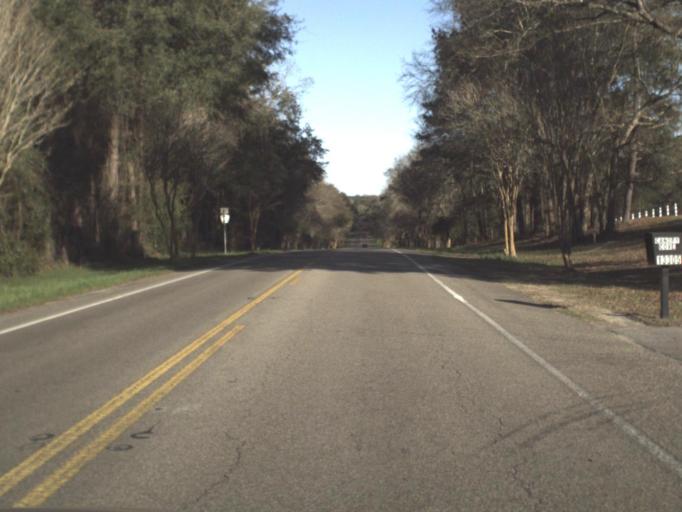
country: US
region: Florida
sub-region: Jefferson County
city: Monticello
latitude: 30.5199
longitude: -84.0520
